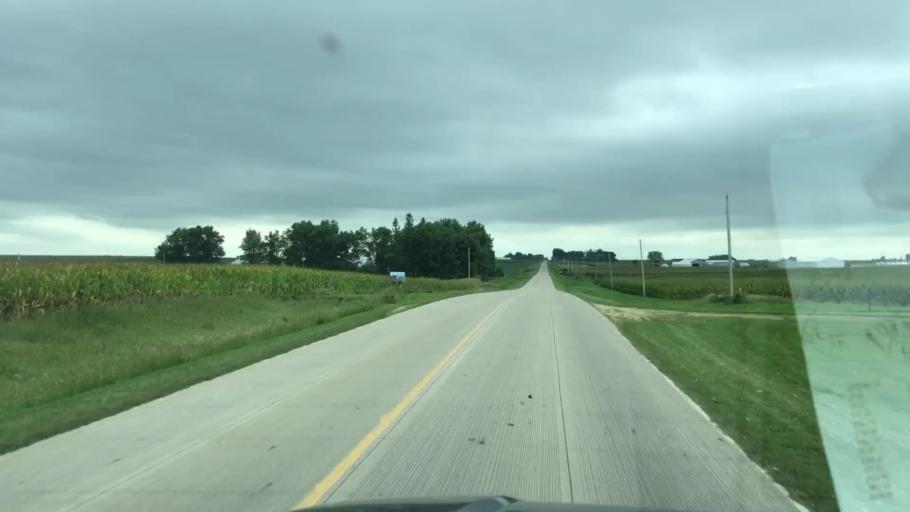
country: US
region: Iowa
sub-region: Sioux County
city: Alton
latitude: 43.1082
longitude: -95.9786
